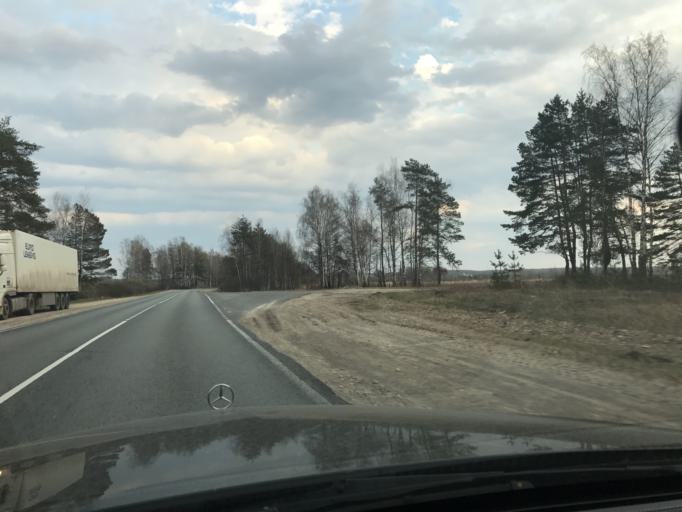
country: RU
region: Vladimir
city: Murom
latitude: 55.6336
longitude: 41.8752
